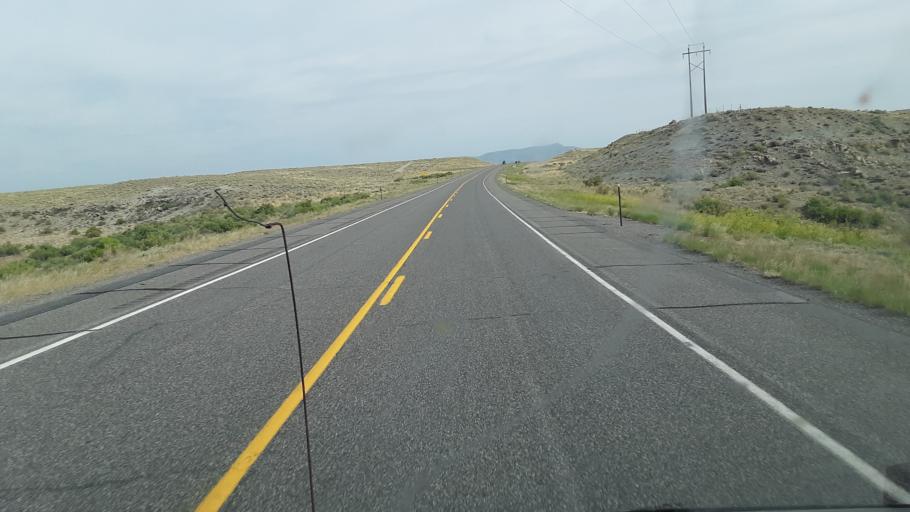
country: US
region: Wyoming
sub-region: Fremont County
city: Riverton
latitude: 43.2843
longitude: -108.1251
